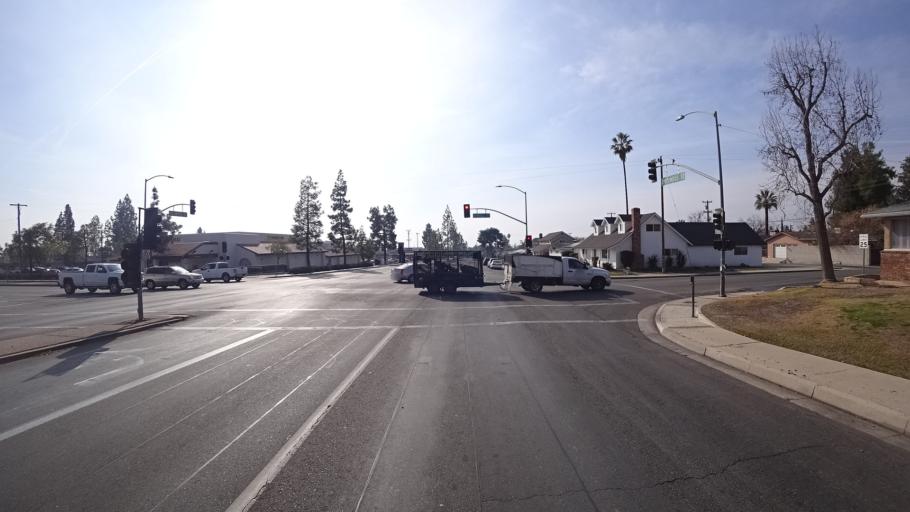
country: US
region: California
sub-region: Kern County
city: Oildale
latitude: 35.4008
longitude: -118.9507
